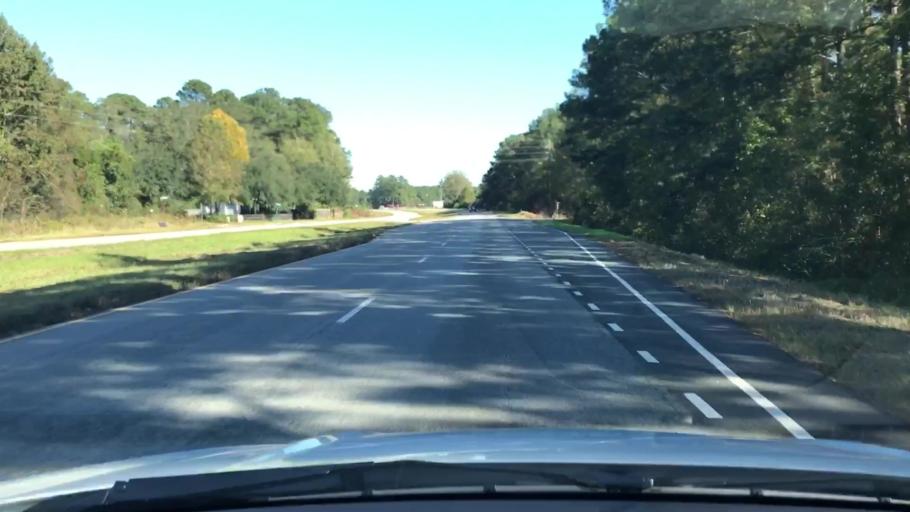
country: US
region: South Carolina
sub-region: Charleston County
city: Ravenel
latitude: 32.7596
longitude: -80.3975
